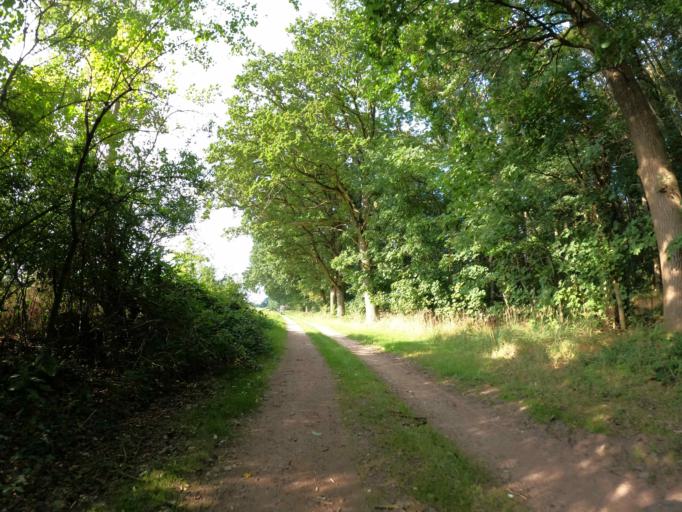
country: DE
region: Mecklenburg-Vorpommern
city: Klink
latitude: 53.4461
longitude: 12.5251
